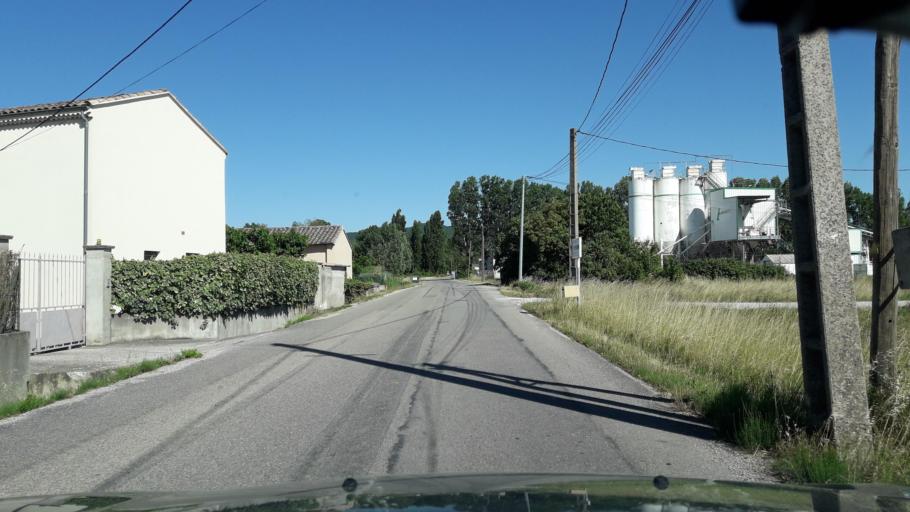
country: FR
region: Rhone-Alpes
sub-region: Departement de la Drome
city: Loriol-sur-Drome
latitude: 44.7493
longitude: 4.7958
